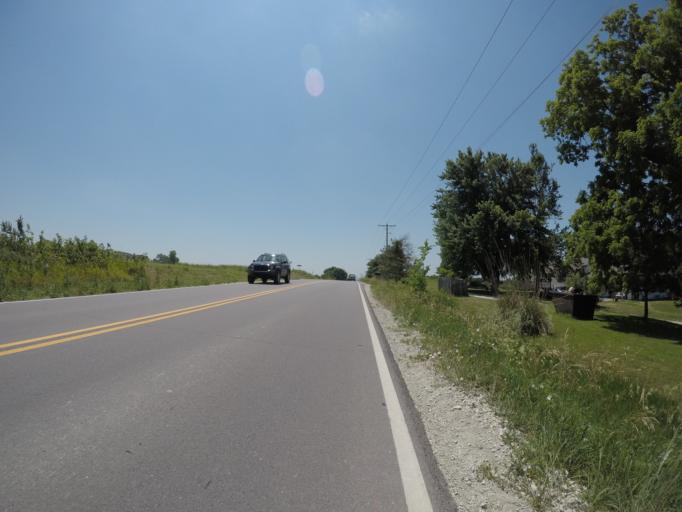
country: US
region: Kansas
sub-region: Riley County
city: Manhattan
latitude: 39.2083
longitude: -96.4404
